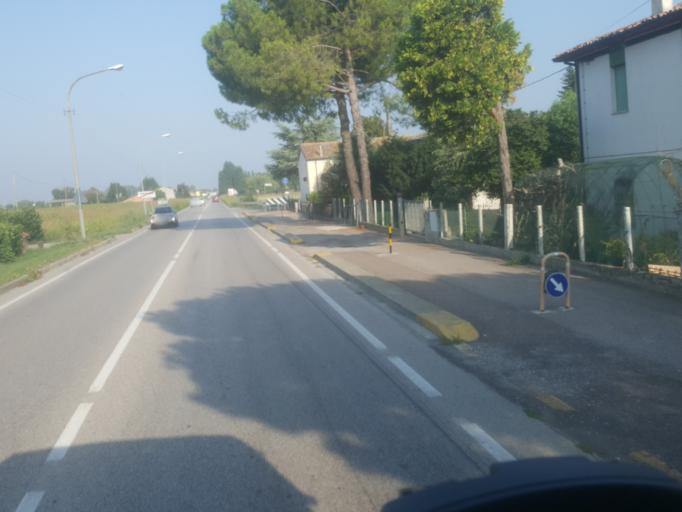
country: IT
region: Emilia-Romagna
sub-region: Provincia di Ravenna
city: Fornace Zarattini
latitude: 44.4496
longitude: 12.1205
